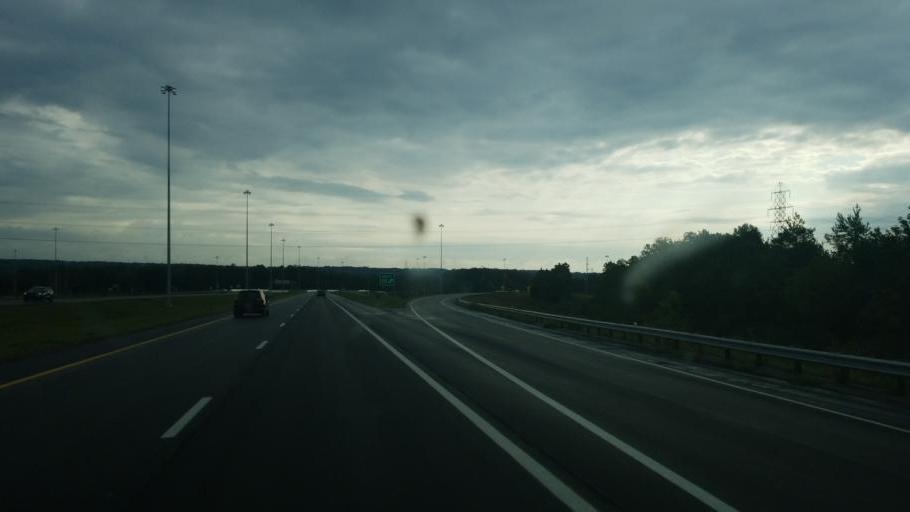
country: US
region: Ohio
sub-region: Summit County
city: Richfield
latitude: 41.2262
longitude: -81.6323
